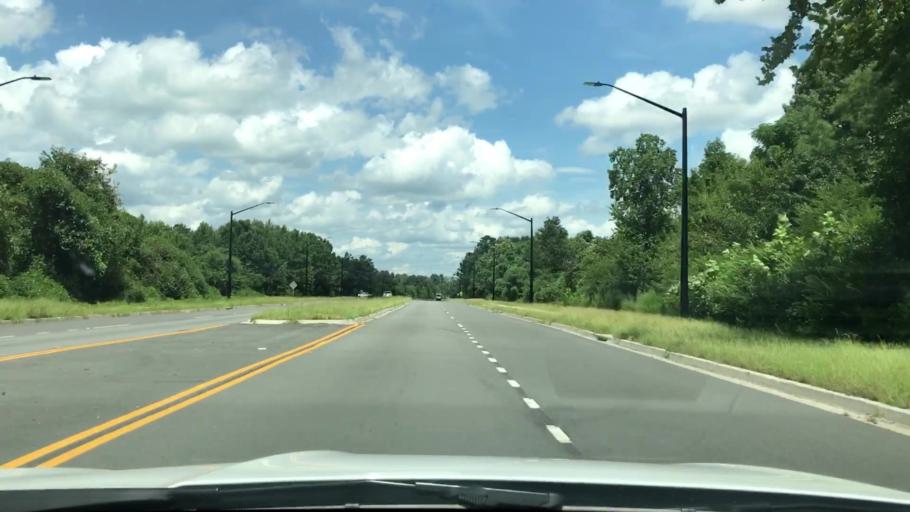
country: US
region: South Carolina
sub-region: Dorchester County
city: Summerville
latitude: 33.0407
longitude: -80.1832
